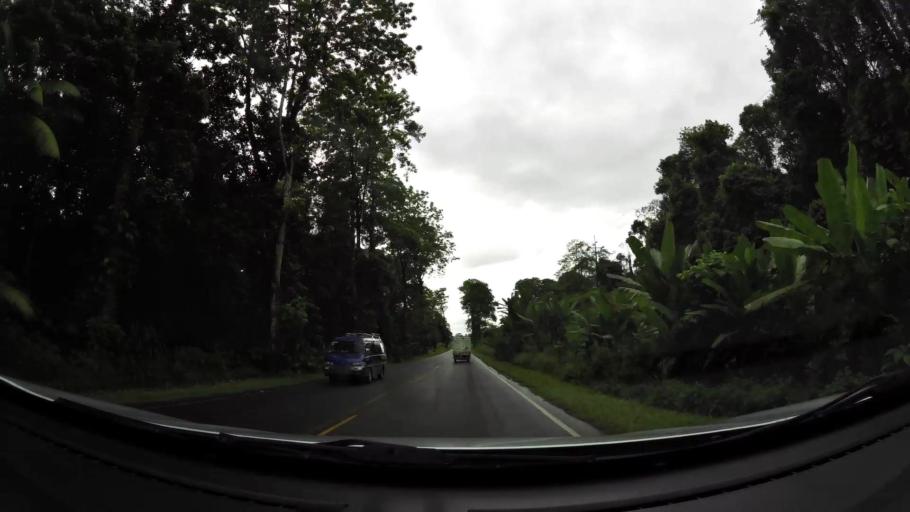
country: CR
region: Limon
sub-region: Canton de Siquirres
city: Siquirres
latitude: 10.1226
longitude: -83.5542
